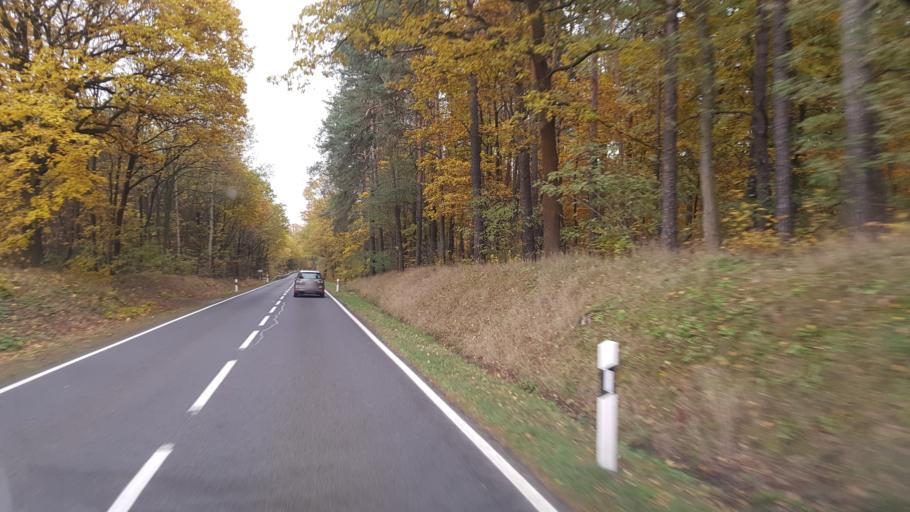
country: DE
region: Brandenburg
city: Crinitz
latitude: 51.7384
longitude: 13.7365
